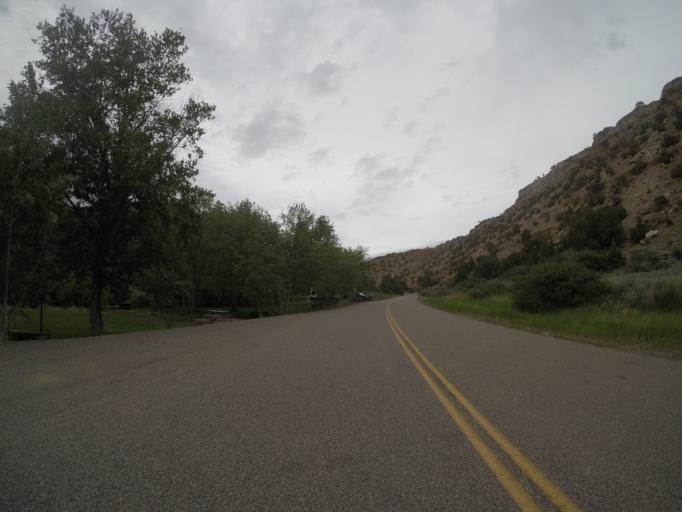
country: US
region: Wyoming
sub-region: Big Horn County
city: Lovell
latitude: 45.1042
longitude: -108.2251
